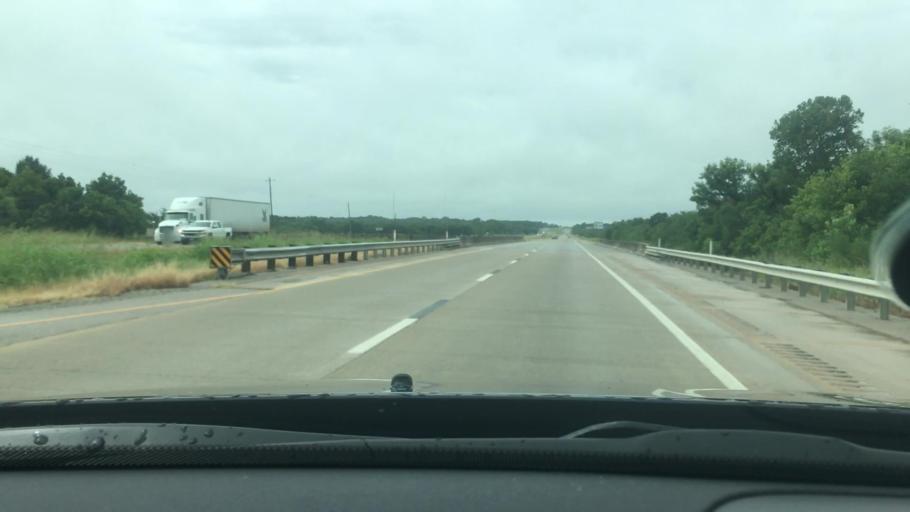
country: US
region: Oklahoma
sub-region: Atoka County
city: Atoka
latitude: 34.2566
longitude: -96.2129
